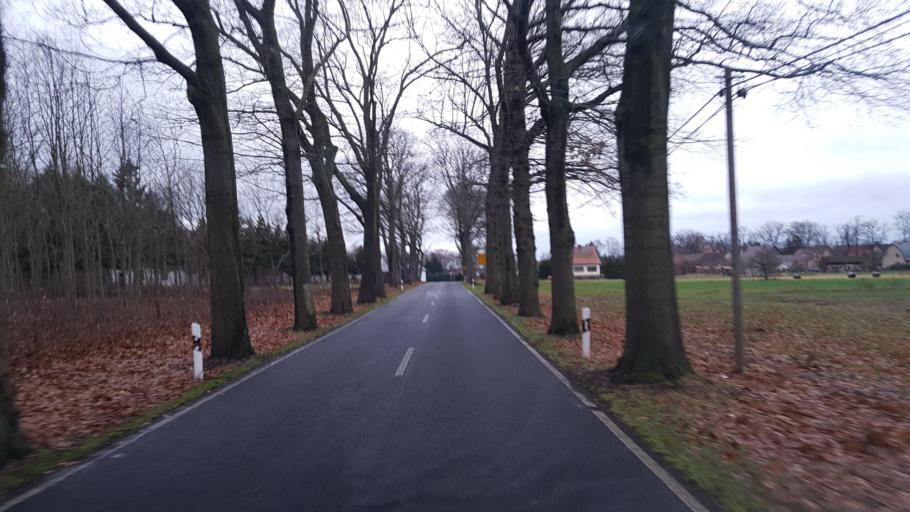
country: DE
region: Brandenburg
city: Tauche
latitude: 52.0754
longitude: 14.0616
